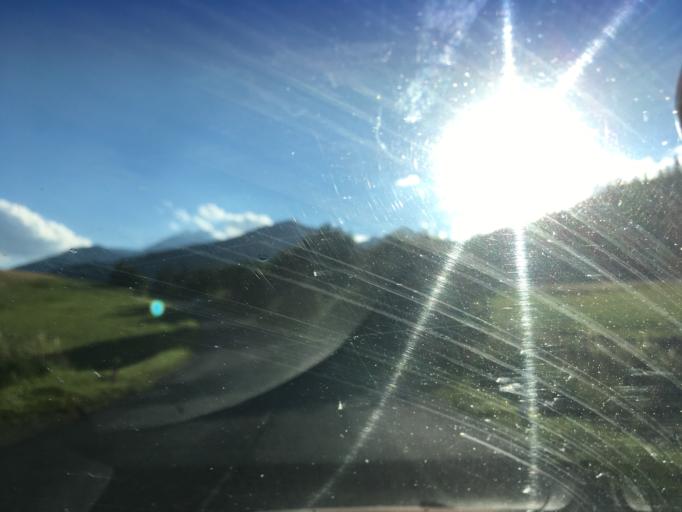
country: SK
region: Presovsky
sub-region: Okres Poprad
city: Zdiar
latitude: 49.2340
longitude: 20.3391
